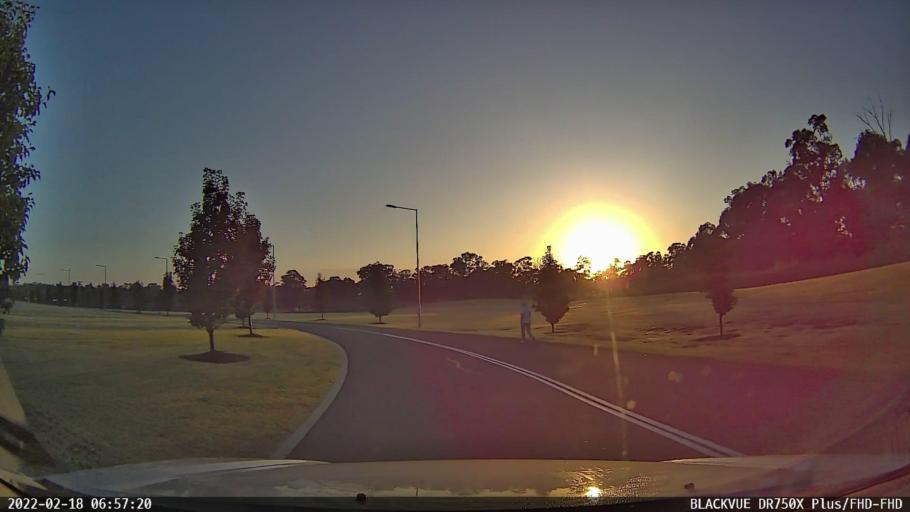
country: AU
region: New South Wales
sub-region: Penrith Municipality
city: Kingswood Park
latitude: -33.7719
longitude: 150.7297
